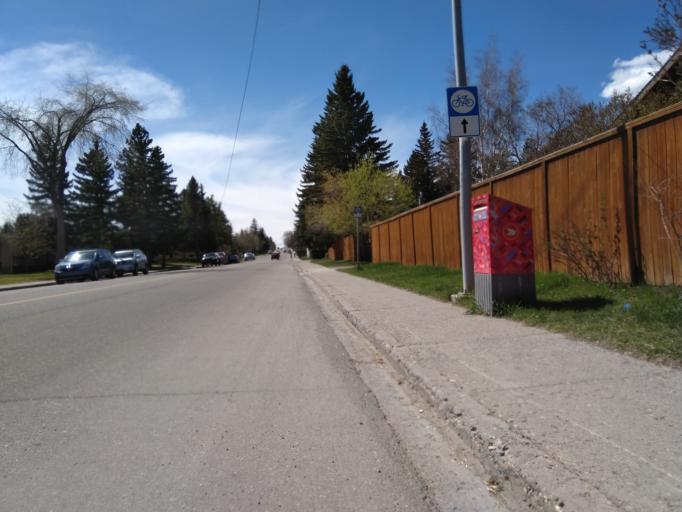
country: CA
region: Alberta
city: Calgary
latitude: 51.0126
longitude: -114.1455
